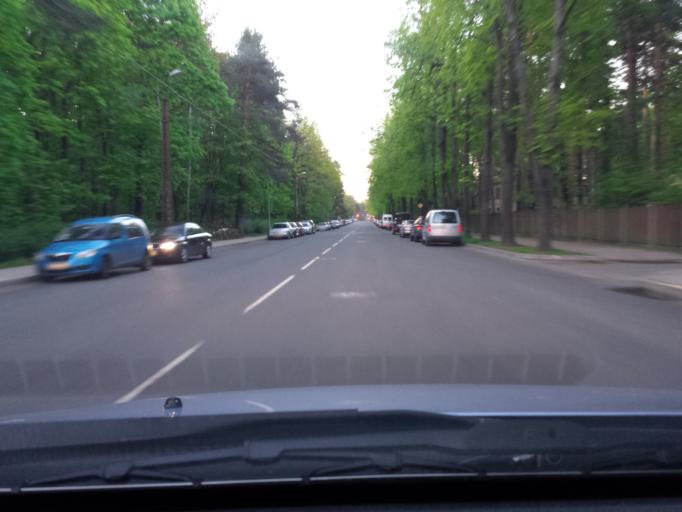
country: LV
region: Riga
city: Jaunciems
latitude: 57.0024
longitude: 24.1521
